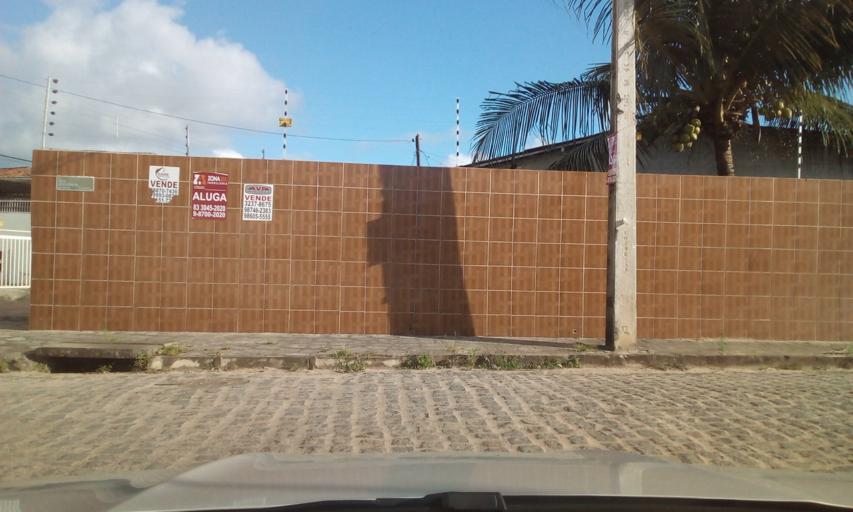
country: BR
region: Paraiba
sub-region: Joao Pessoa
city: Joao Pessoa
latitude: -7.1733
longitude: -34.8637
